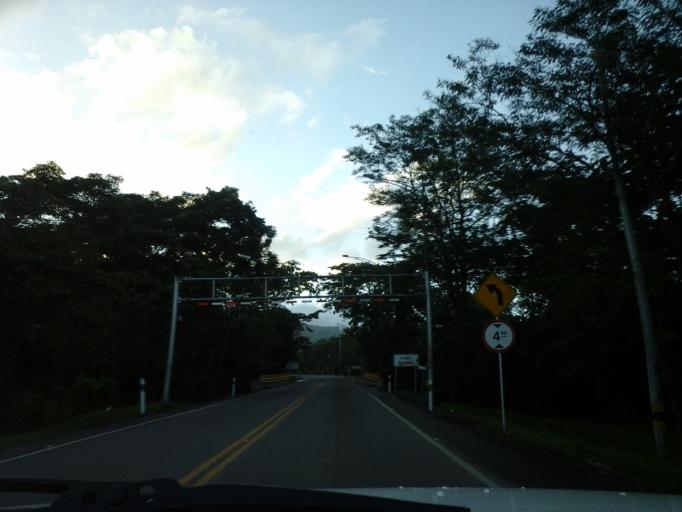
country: CO
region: Meta
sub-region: Villavicencio
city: Villavicencio
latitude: 4.1370
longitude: -73.6560
